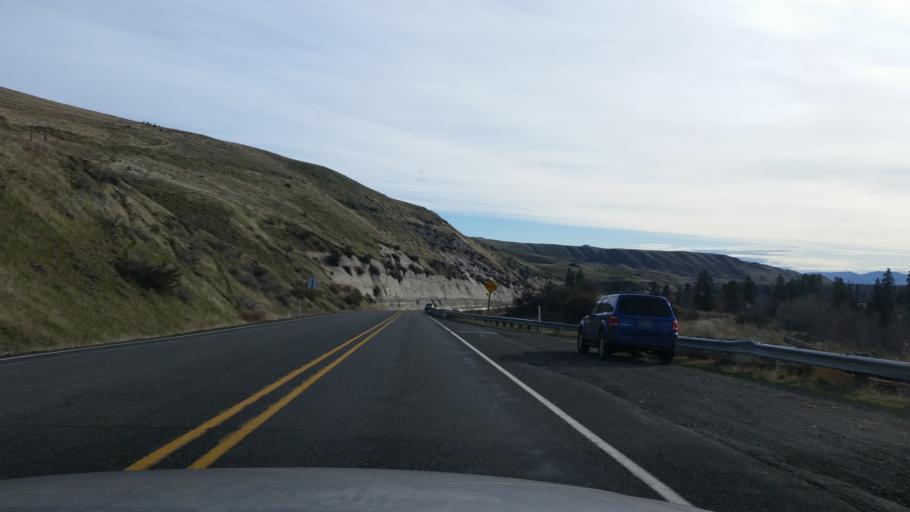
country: US
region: Washington
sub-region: Kittitas County
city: Ellensburg
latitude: 47.1030
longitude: -120.7014
